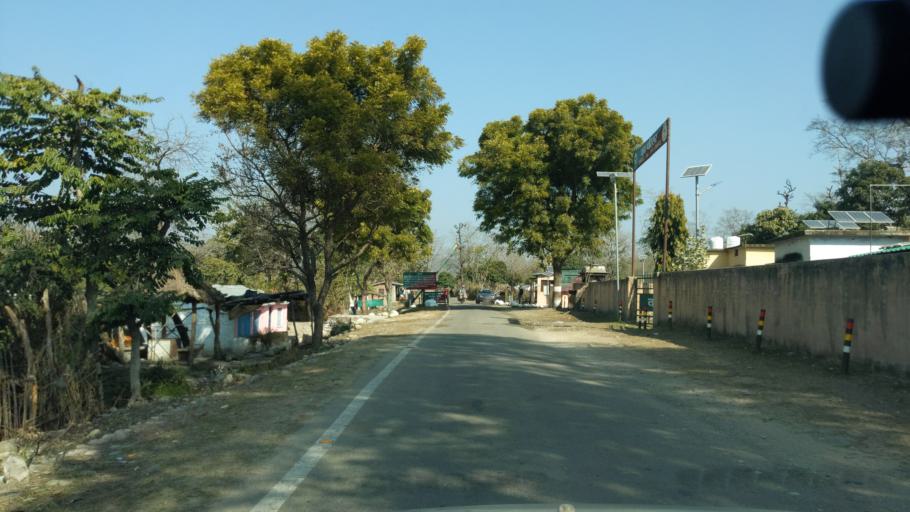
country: IN
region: Uttarakhand
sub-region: Naini Tal
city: Ramnagar
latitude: 29.4212
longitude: 79.1388
